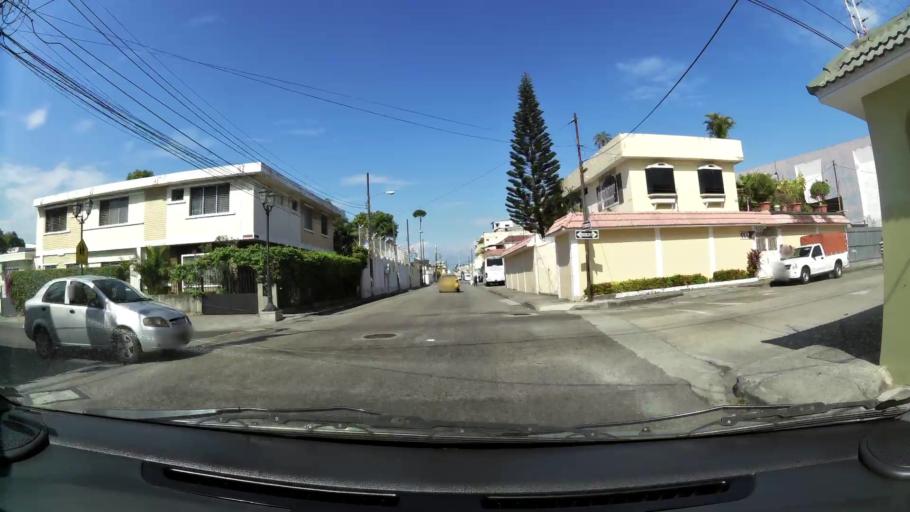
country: EC
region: Guayas
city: Guayaquil
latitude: -2.2212
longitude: -79.8915
